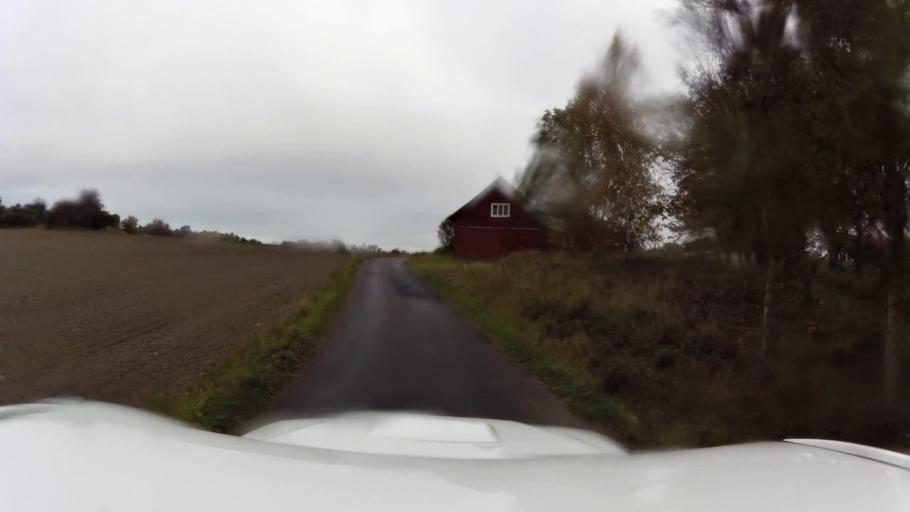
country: SE
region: OEstergoetland
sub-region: Linkopings Kommun
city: Linghem
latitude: 58.4908
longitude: 15.7424
